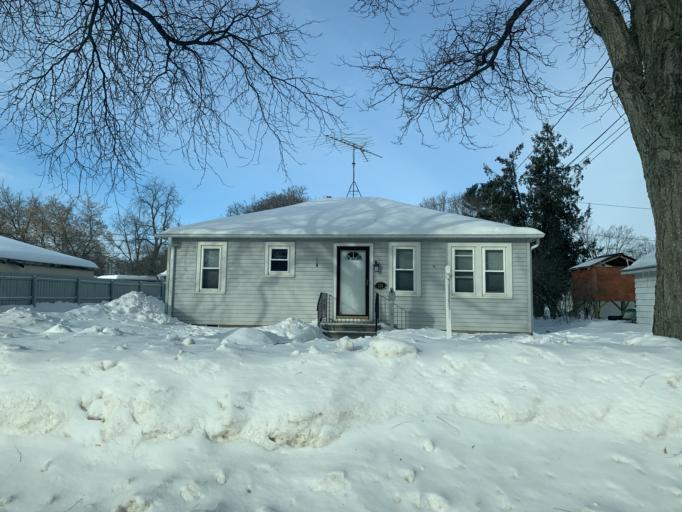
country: US
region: Wisconsin
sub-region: Marinette County
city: Peshtigo
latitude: 45.0524
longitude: -87.7402
